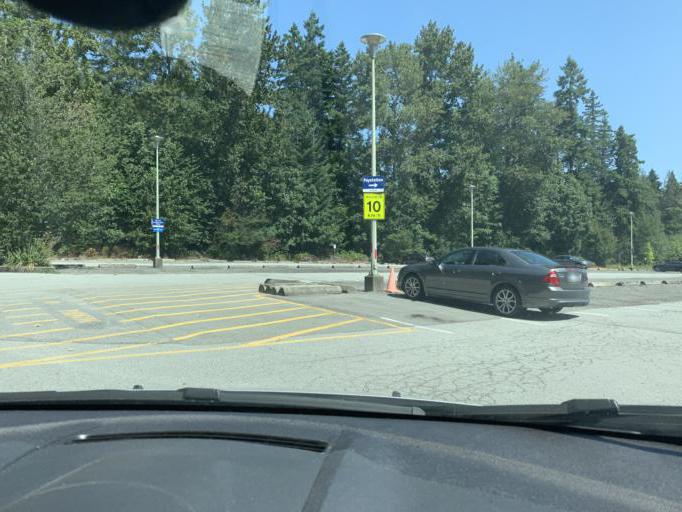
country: CA
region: British Columbia
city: West End
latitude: 49.2484
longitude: -123.2312
